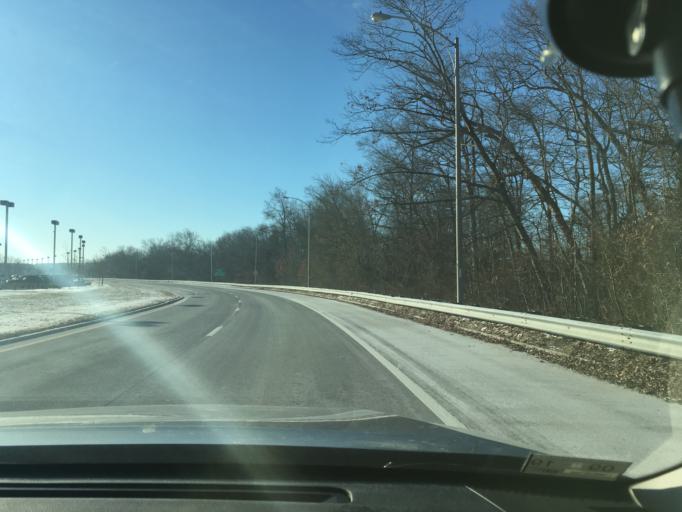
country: US
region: Rhode Island
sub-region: Kent County
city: West Warwick
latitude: 41.7330
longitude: -71.4818
